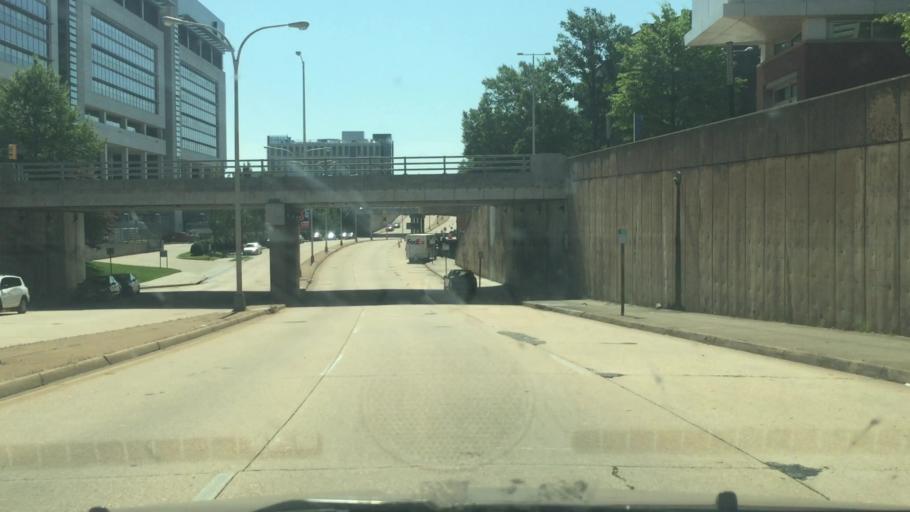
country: US
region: Virginia
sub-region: City of Richmond
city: Richmond
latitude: 37.5460
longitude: -77.4353
